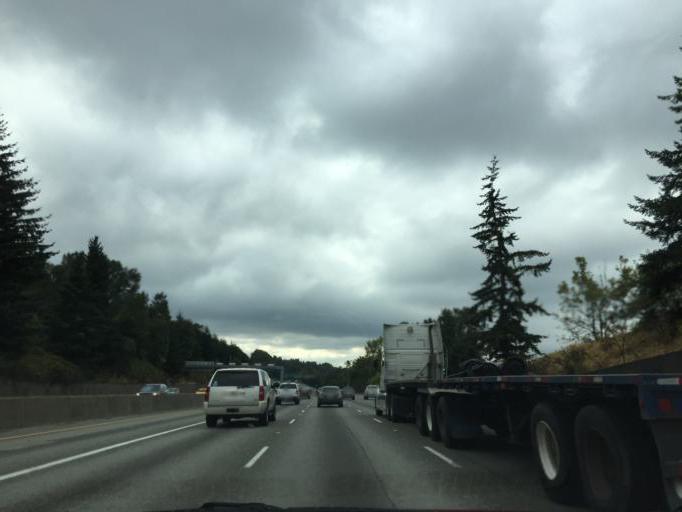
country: US
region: Washington
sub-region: King County
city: Riverton
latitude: 47.4992
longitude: -122.2737
